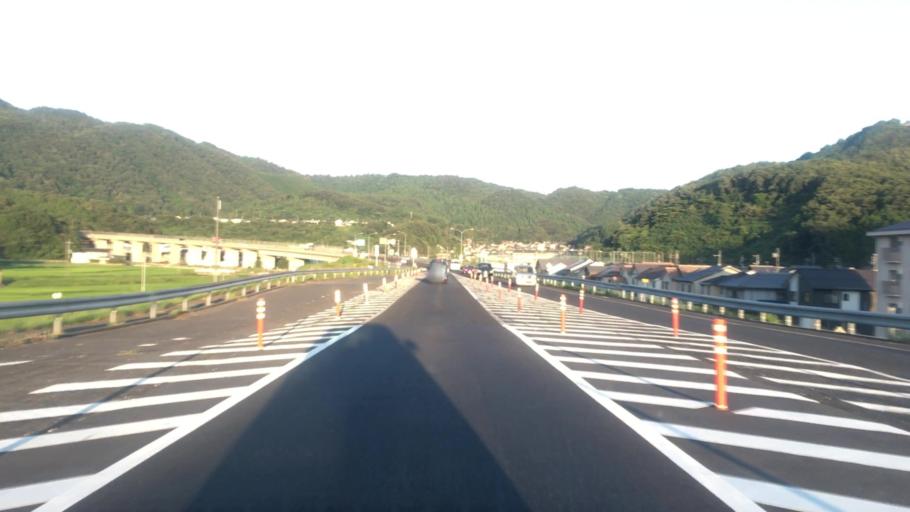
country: JP
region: Tottori
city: Tottori
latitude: 35.5226
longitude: 134.2294
